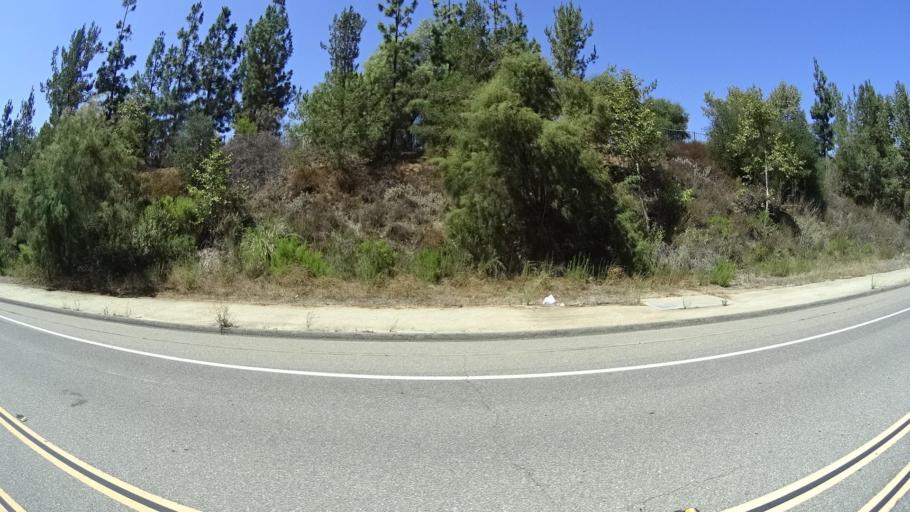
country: US
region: California
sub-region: San Diego County
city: Bonsall
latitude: 33.3163
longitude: -117.1950
